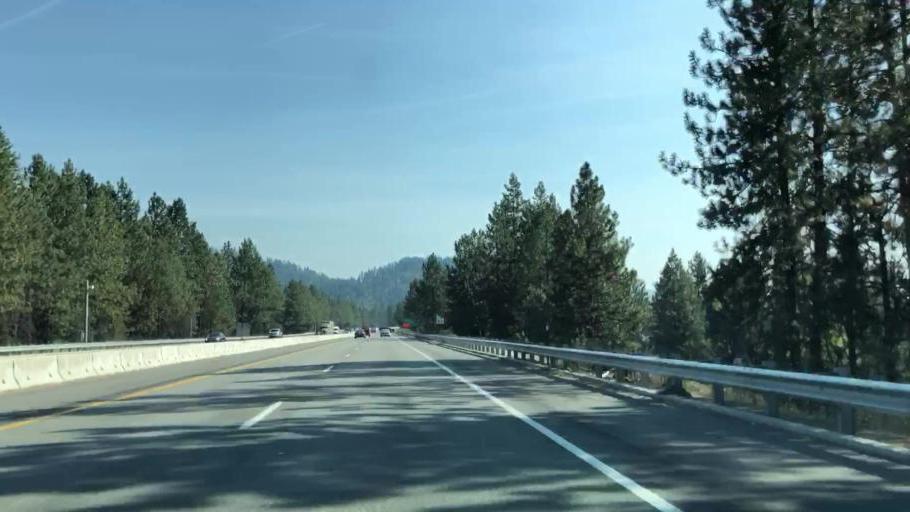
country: US
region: Idaho
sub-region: Kootenai County
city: Coeur d'Alene
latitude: 47.6812
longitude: -116.7576
